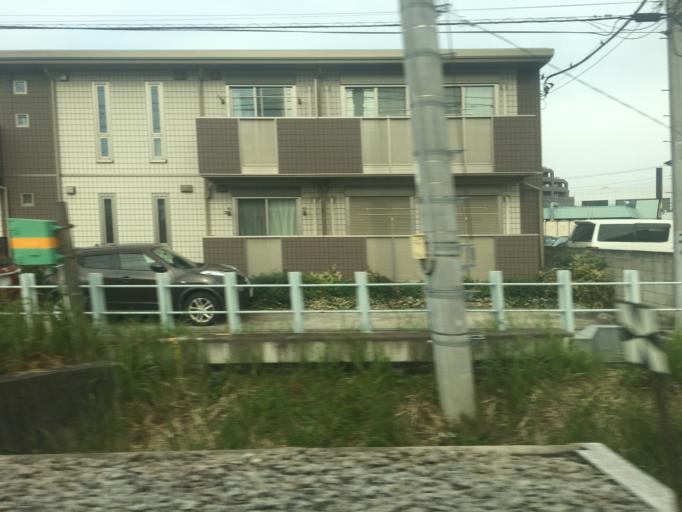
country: JP
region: Saitama
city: Kawagoe
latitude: 35.9073
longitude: 139.4771
